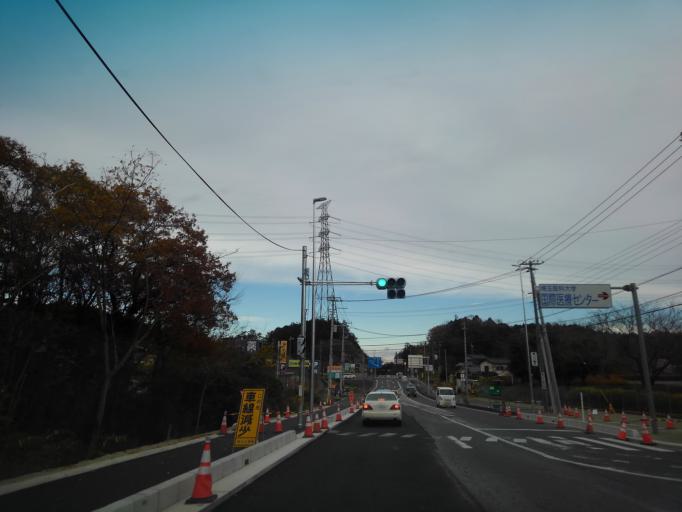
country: JP
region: Saitama
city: Morohongo
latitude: 35.9215
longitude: 139.3201
